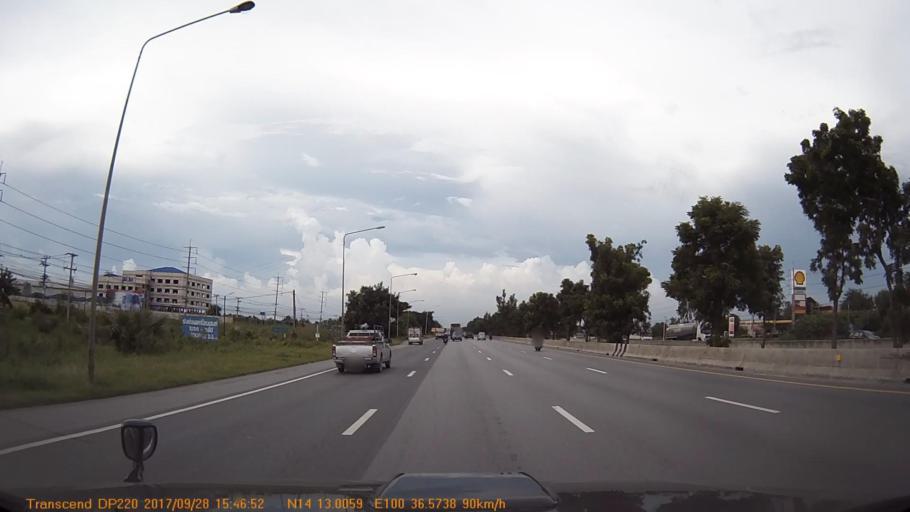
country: TH
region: Phra Nakhon Si Ayutthaya
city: Bang Pa-in
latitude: 14.2171
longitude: 100.6096
